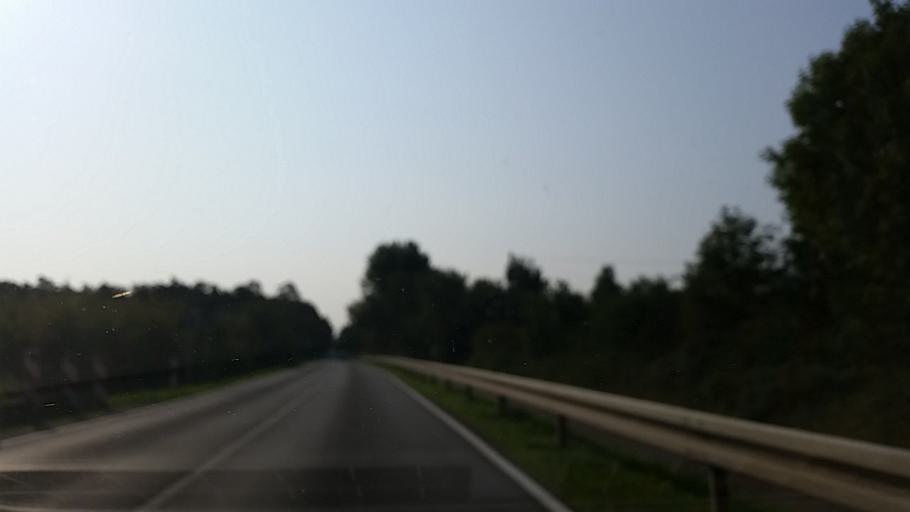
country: DE
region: Mecklenburg-Vorpommern
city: Wittenburg
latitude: 53.4960
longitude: 11.0960
